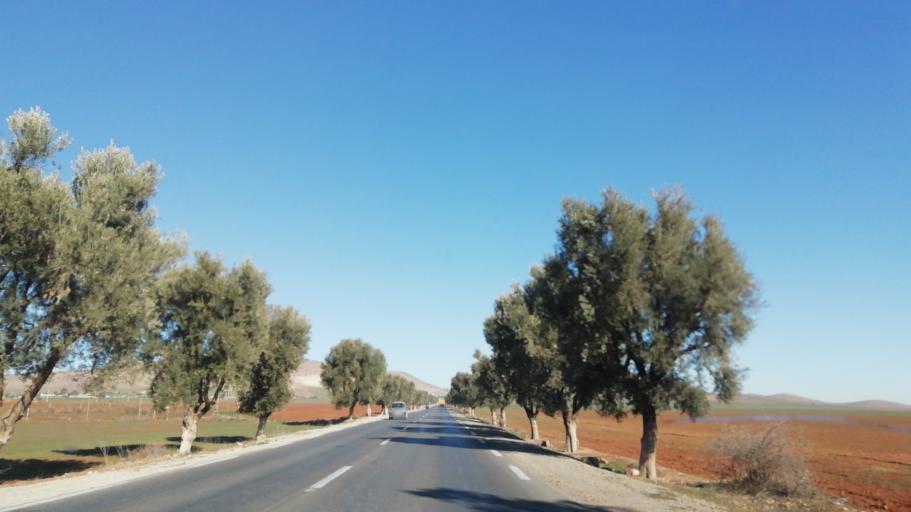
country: DZ
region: Mascara
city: Mascara
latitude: 35.2205
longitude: 0.1131
